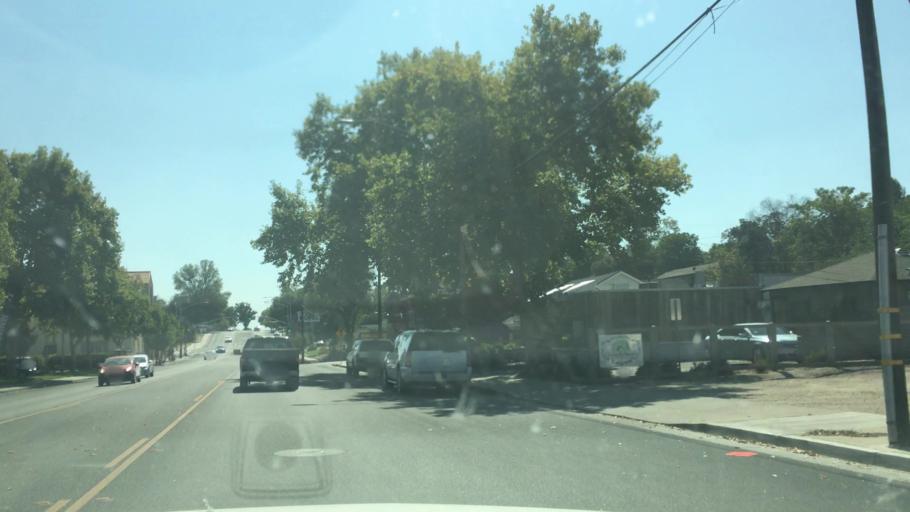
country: US
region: California
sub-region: San Luis Obispo County
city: Paso Robles
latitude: 35.6202
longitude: -120.6909
